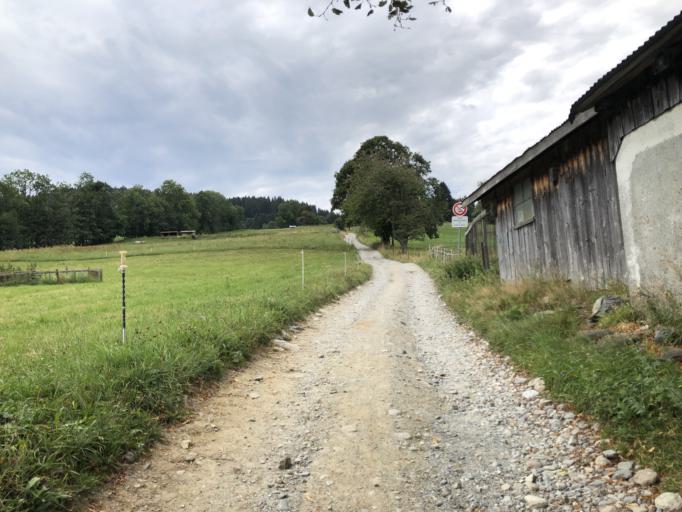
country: FR
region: Rhone-Alpes
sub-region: Departement de la Haute-Savoie
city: Combloux
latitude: 45.8856
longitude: 6.6335
